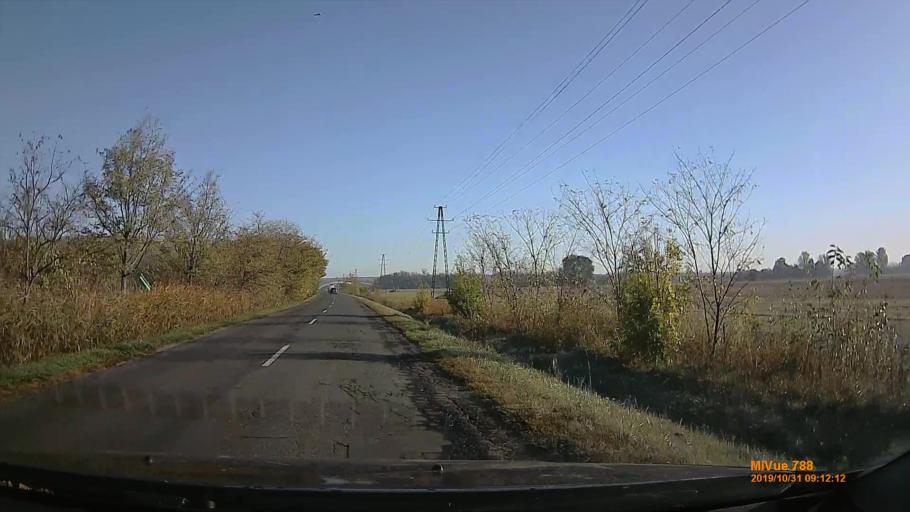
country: HU
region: Pest
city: Peteri
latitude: 47.3720
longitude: 19.3926
